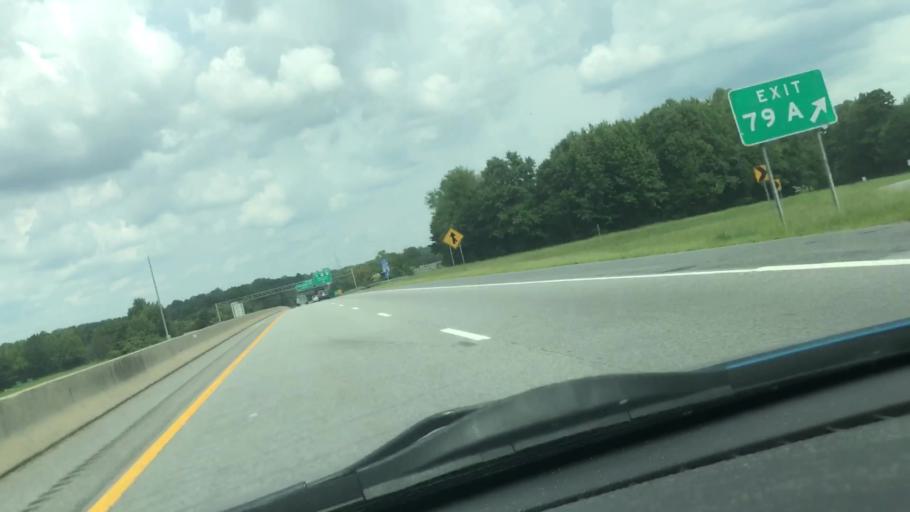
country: US
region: North Carolina
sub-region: Guilford County
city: Greensboro
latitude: 36.0167
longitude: -79.8262
